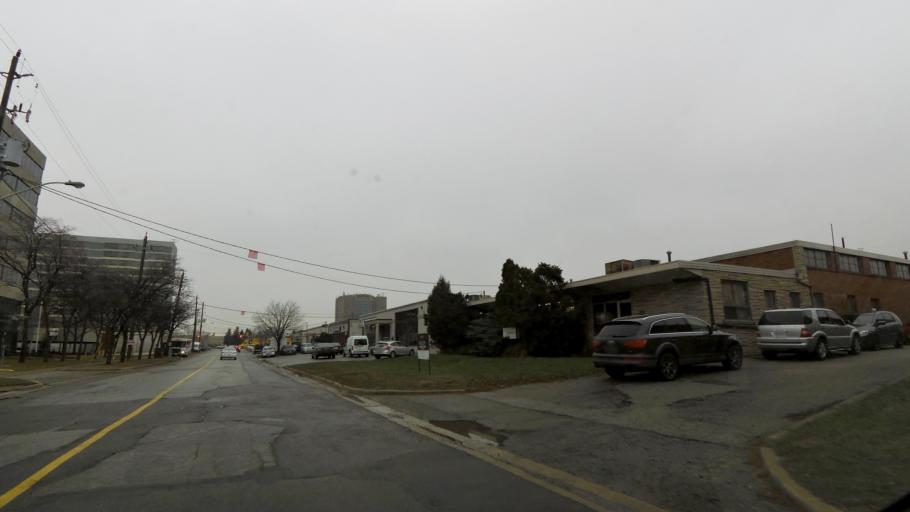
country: CA
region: Ontario
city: Etobicoke
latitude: 43.6885
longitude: -79.5763
